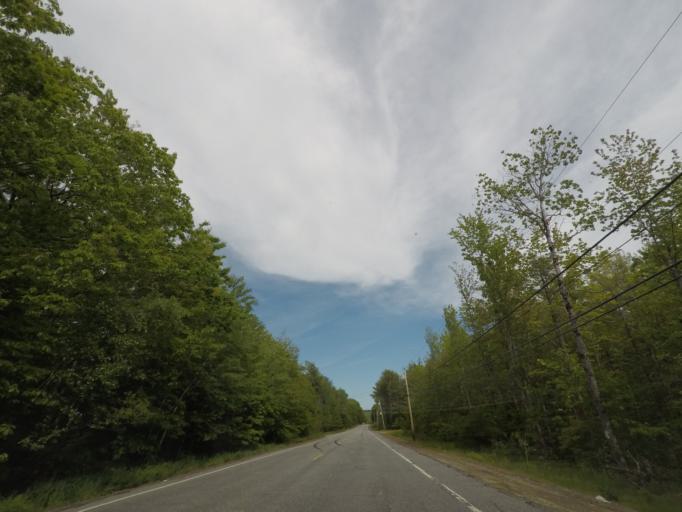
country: US
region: Maine
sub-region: Sagadahoc County
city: Richmond
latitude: 44.0867
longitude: -69.7649
